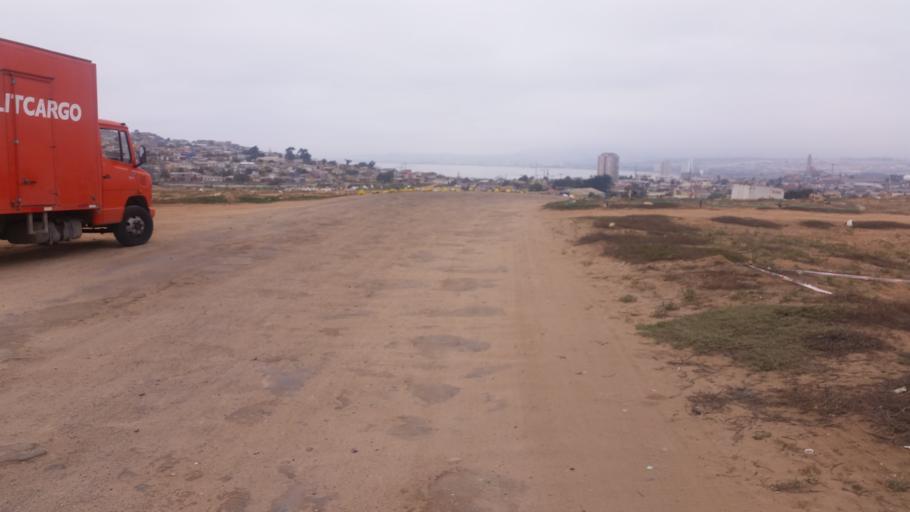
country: CL
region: Coquimbo
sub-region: Provincia de Elqui
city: Coquimbo
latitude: -29.9623
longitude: -71.3540
